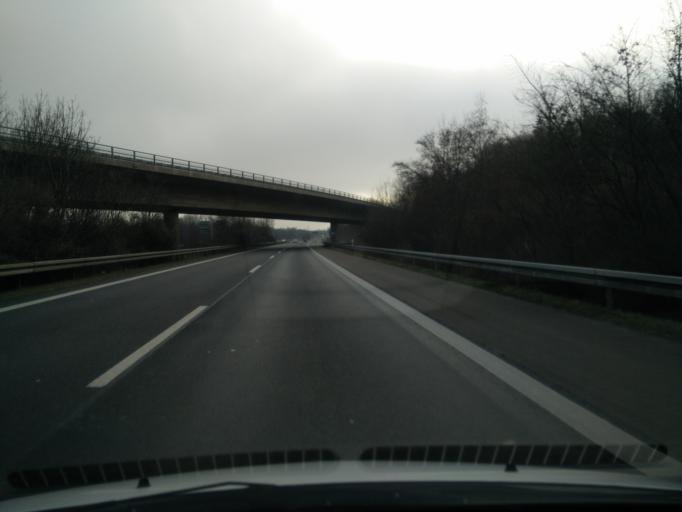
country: DE
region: Bavaria
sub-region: Upper Bavaria
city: Unterfoehring
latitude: 48.2192
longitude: 11.6328
